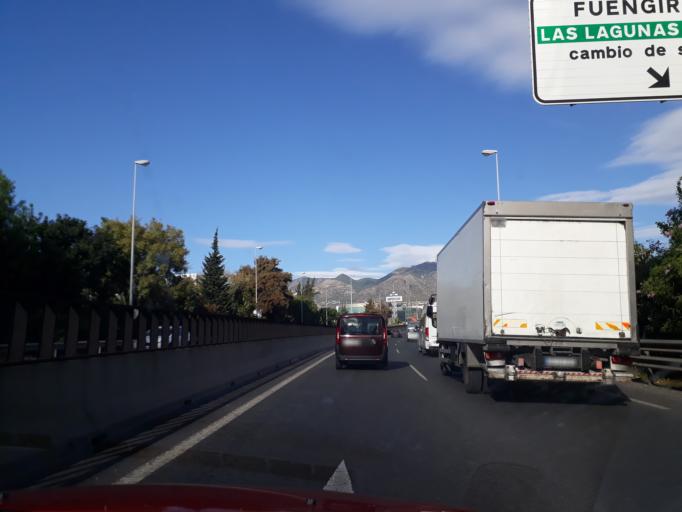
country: ES
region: Andalusia
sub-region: Provincia de Malaga
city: Fuengirola
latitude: 36.5434
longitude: -4.6344
